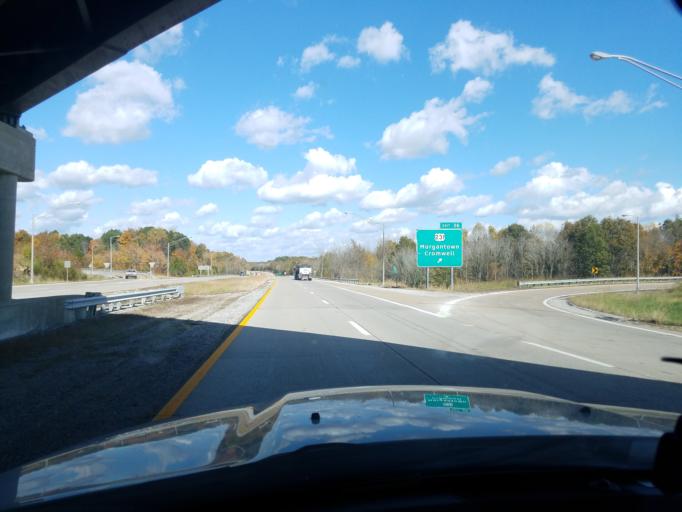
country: US
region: Kentucky
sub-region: Ohio County
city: Oak Grove
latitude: 37.2982
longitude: -86.7389
